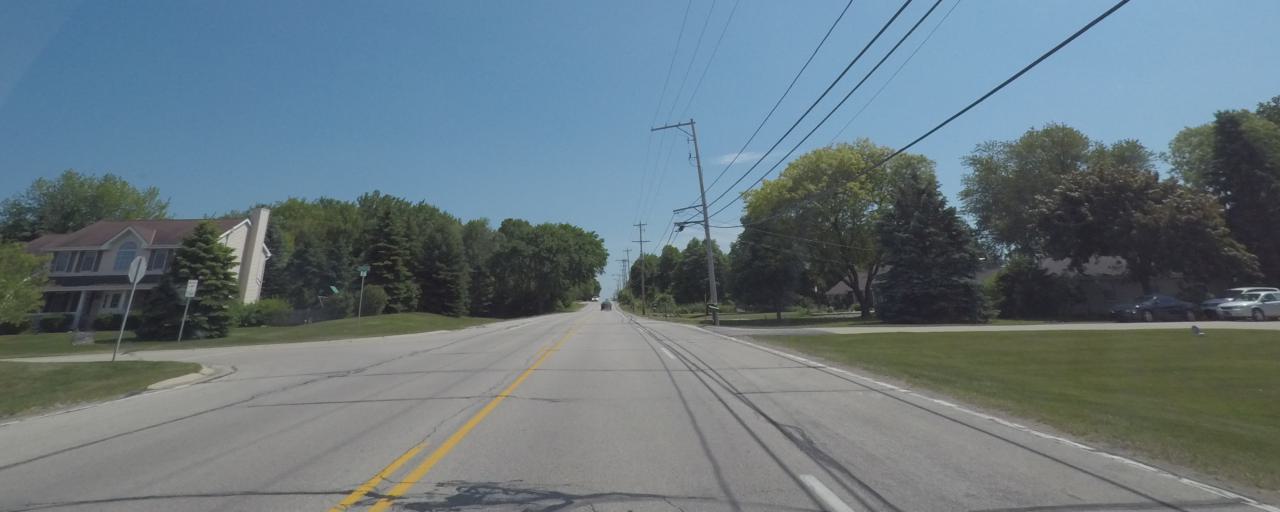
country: US
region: Wisconsin
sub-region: Milwaukee County
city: Oak Creek
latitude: 42.8827
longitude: -87.9320
